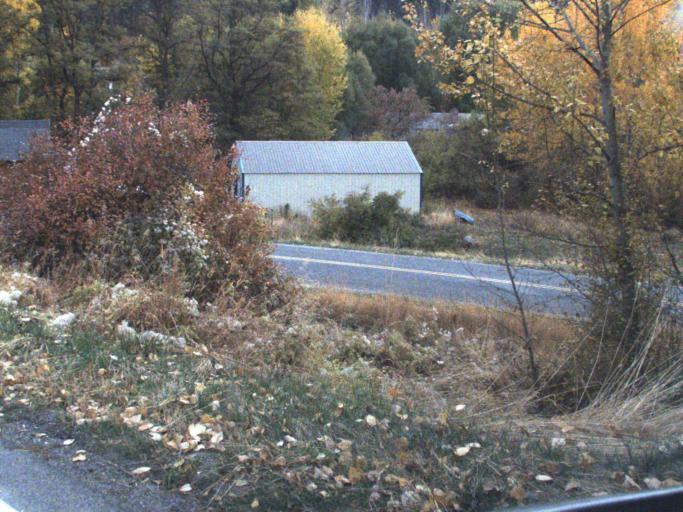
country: US
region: Washington
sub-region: Lincoln County
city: Davenport
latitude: 48.1181
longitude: -118.2031
